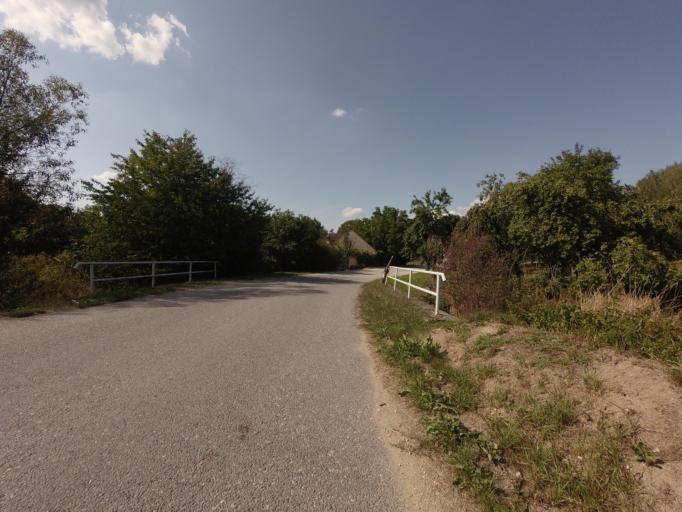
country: CZ
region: Jihocesky
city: Tyn nad Vltavou
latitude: 49.1728
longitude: 14.4201
